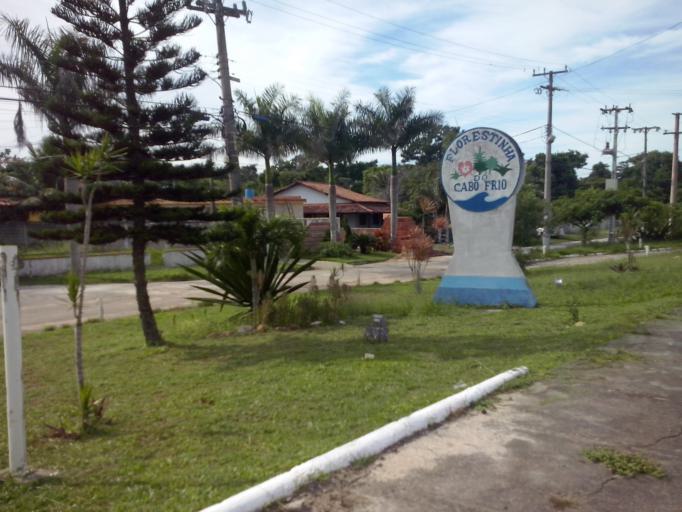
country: BR
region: Rio de Janeiro
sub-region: Armacao De Buzios
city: Armacao de Buzios
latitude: -22.6815
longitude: -42.0072
